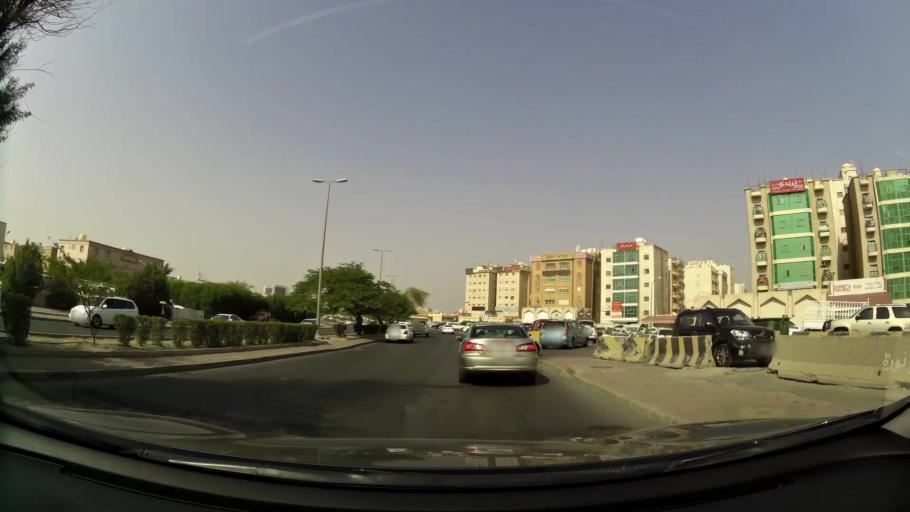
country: KW
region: Muhafazat al Jahra'
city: Al Jahra'
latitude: 29.3402
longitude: 47.6676
